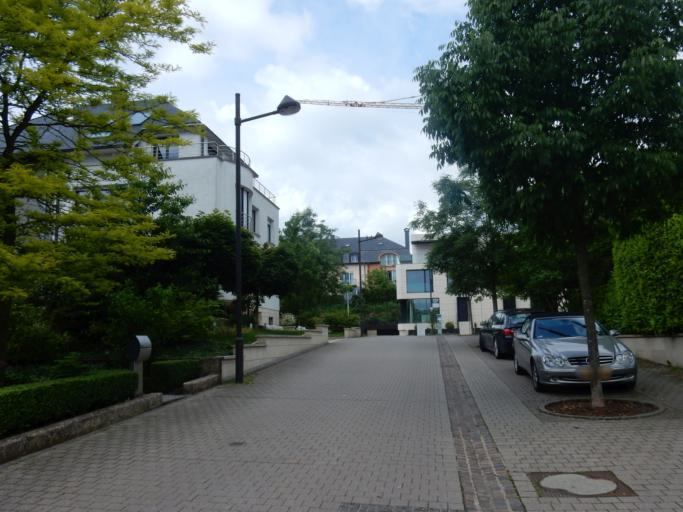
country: LU
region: Luxembourg
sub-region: Canton de Luxembourg
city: Strassen
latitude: 49.6067
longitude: 6.0990
